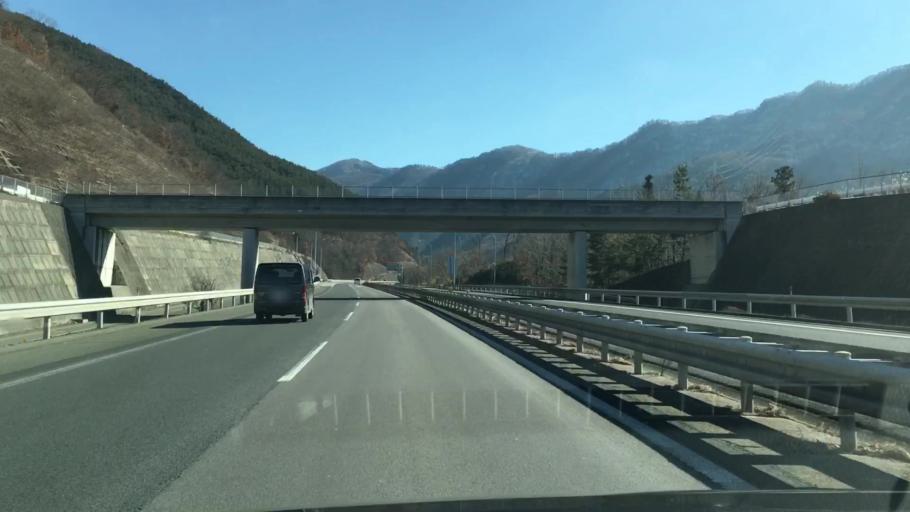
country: JP
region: Nagano
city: Ueda
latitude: 36.4448
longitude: 138.2091
